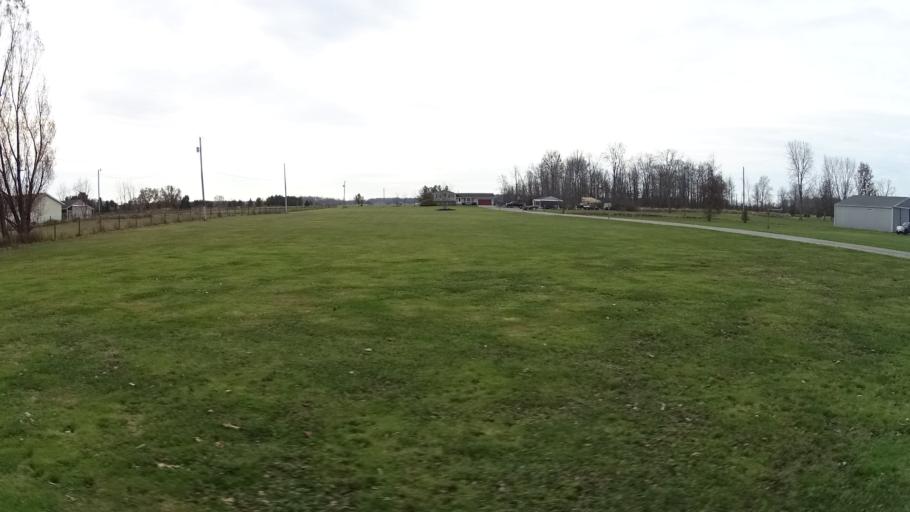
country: US
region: Ohio
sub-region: Lorain County
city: Lagrange
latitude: 41.1998
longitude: -82.1439
